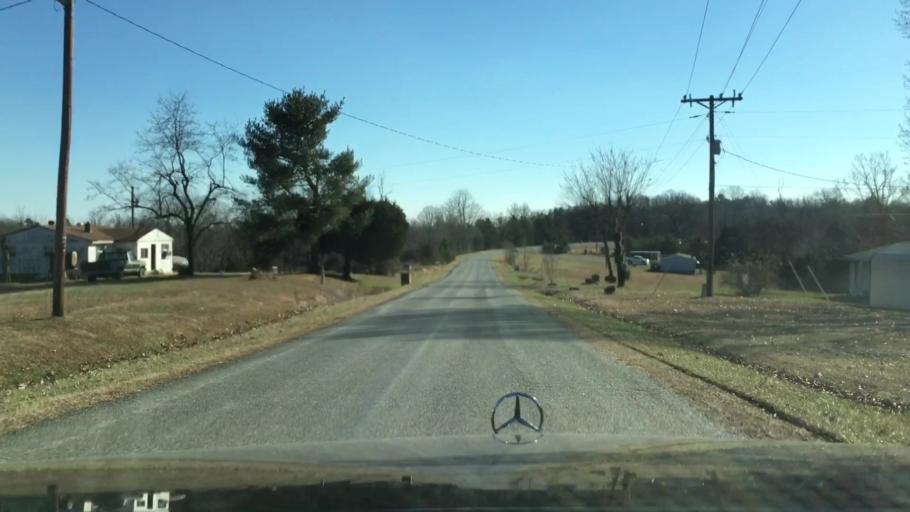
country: US
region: Virginia
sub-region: Campbell County
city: Altavista
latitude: 37.1640
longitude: -79.3602
